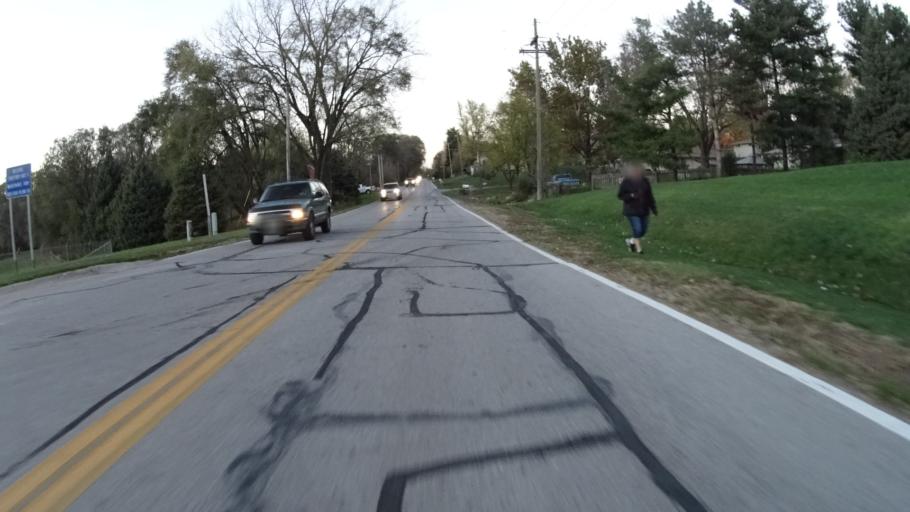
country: US
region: Nebraska
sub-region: Sarpy County
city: Offutt Air Force Base
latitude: 41.1769
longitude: -95.9527
